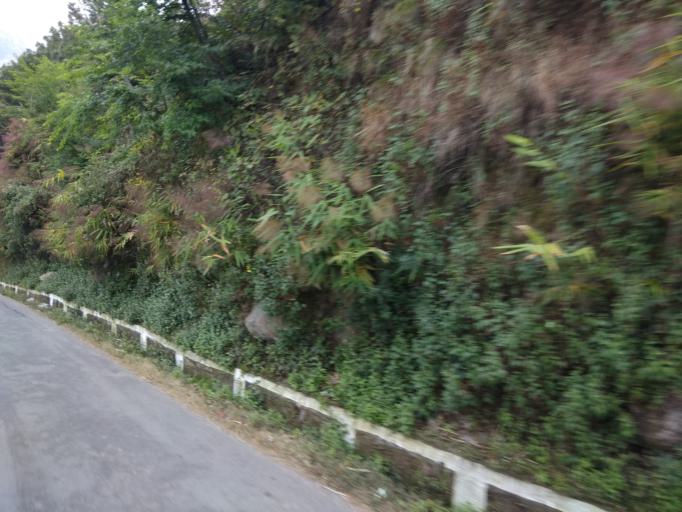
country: IN
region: Himachal Pradesh
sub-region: Kangra
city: Dharmsala
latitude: 32.1601
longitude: 76.4063
